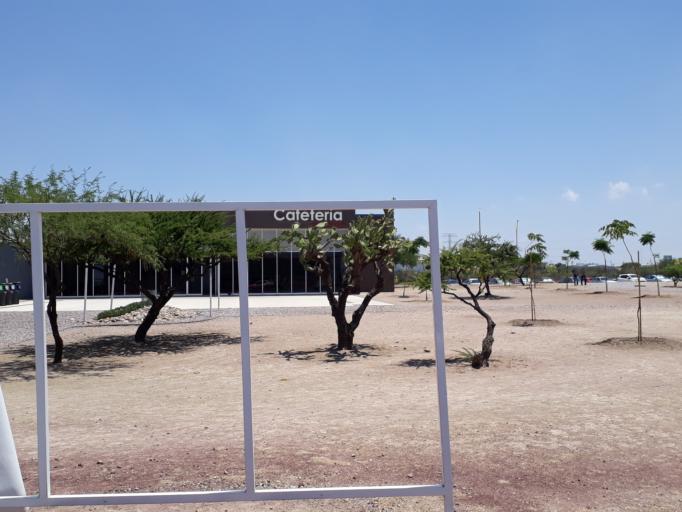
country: MX
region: Aguascalientes
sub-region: Aguascalientes
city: San Sebastian [Fraccionamiento]
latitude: 21.7930
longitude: -102.2917
